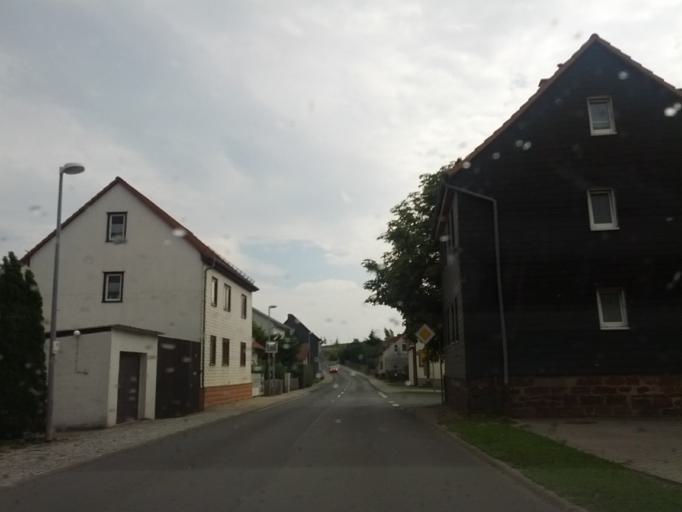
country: DE
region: Thuringia
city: Ernstroda
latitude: 50.8578
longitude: 10.6427
